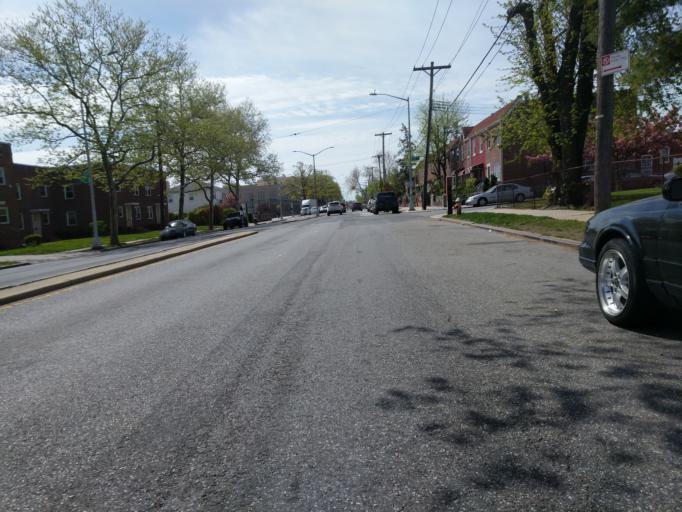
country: US
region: New York
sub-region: Nassau County
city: Bellerose Terrace
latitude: 40.7005
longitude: -73.7482
